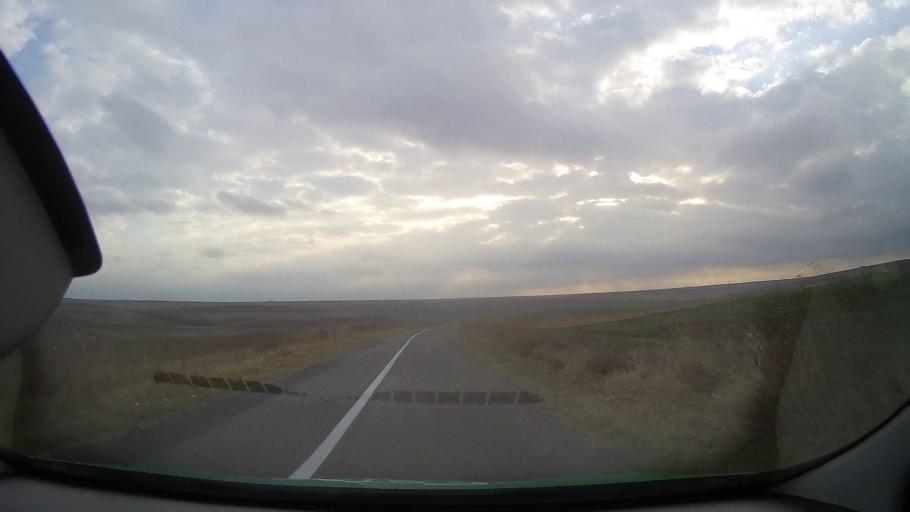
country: RO
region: Constanta
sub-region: Comuna Deleni
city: Pietreni
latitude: 44.1202
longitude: 28.1039
